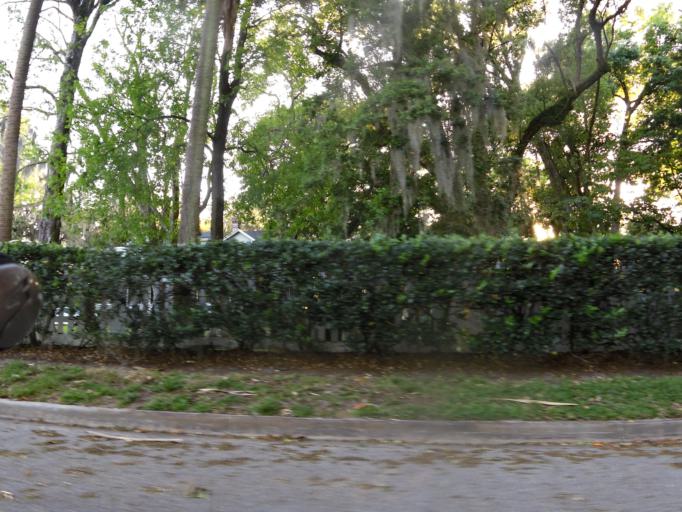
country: US
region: Florida
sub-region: Duval County
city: Jacksonville
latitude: 30.3098
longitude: -81.6339
